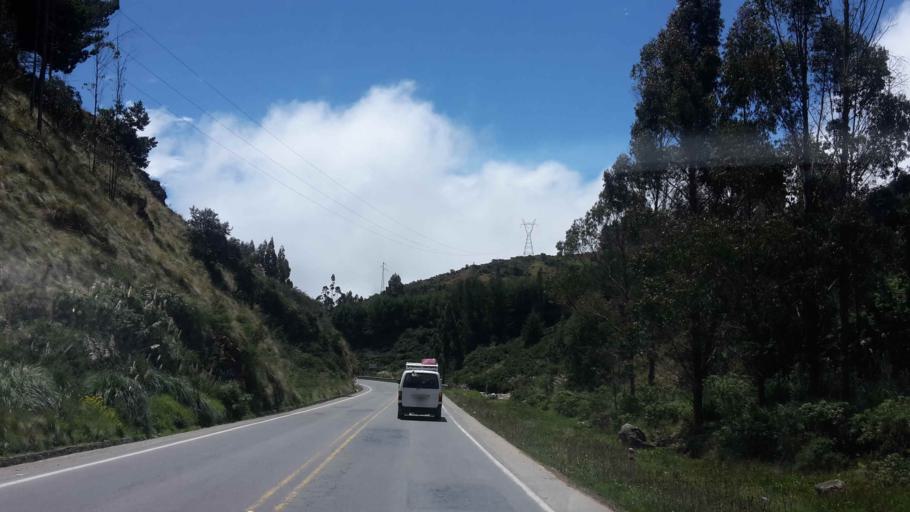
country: BO
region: Cochabamba
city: Colomi
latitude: -17.2707
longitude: -65.8785
